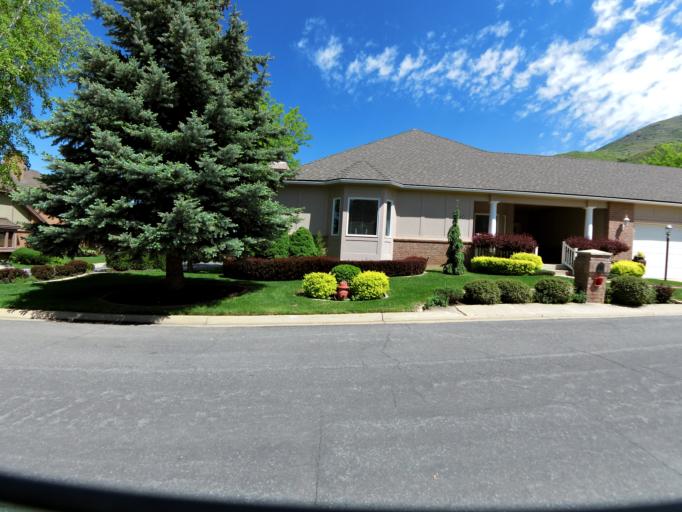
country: US
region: Utah
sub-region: Weber County
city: Uintah
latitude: 41.1763
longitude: -111.9328
